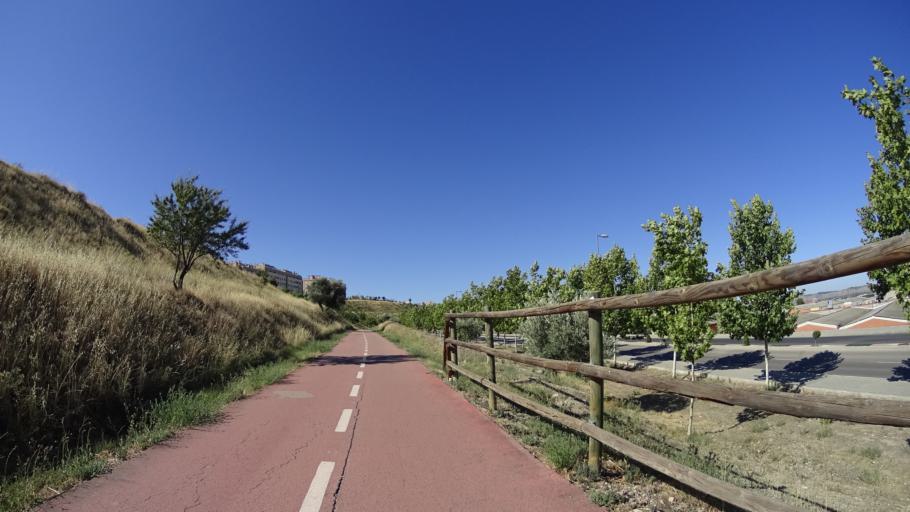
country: ES
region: Madrid
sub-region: Provincia de Madrid
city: Arganda
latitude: 40.3024
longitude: -3.4536
